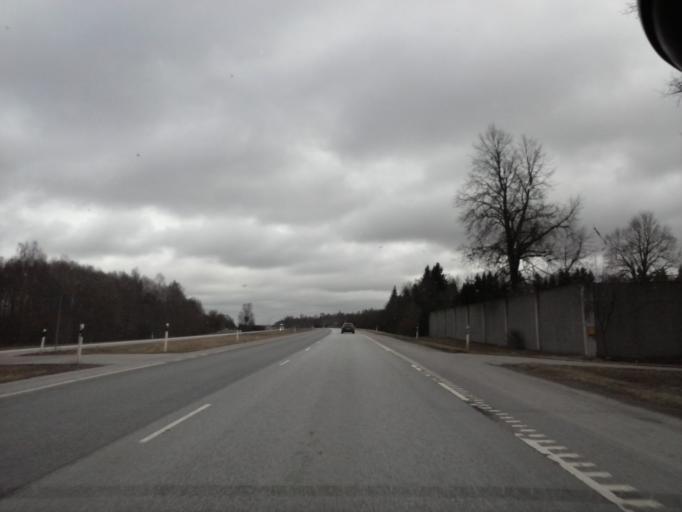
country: EE
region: Harju
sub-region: Rae vald
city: Vaida
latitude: 59.3038
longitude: 24.9448
